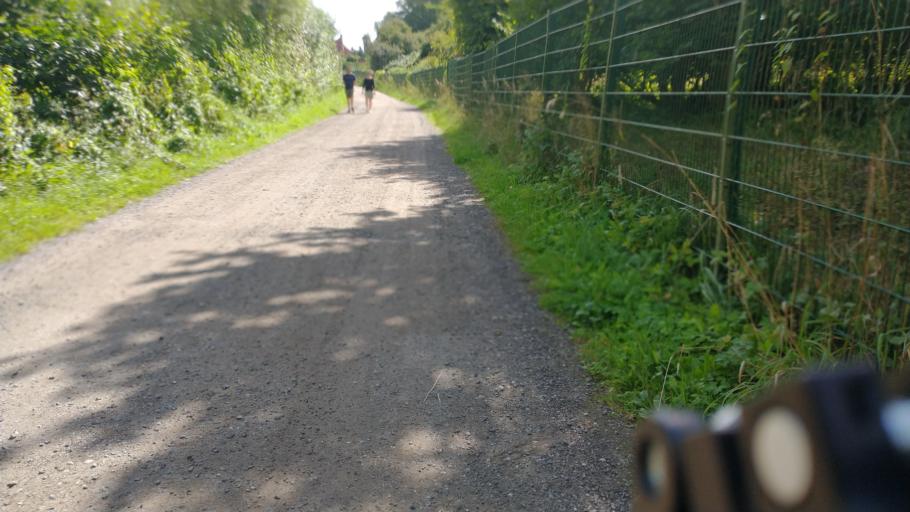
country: DE
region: Schleswig-Holstein
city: Bad Oldesloe
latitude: 53.8146
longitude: 10.3537
